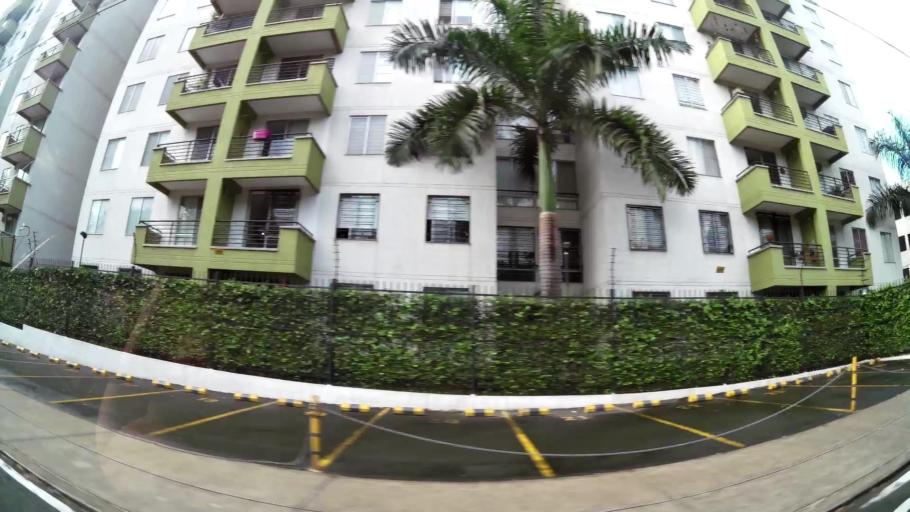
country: CO
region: Valle del Cauca
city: Cali
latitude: 3.4928
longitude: -76.5210
